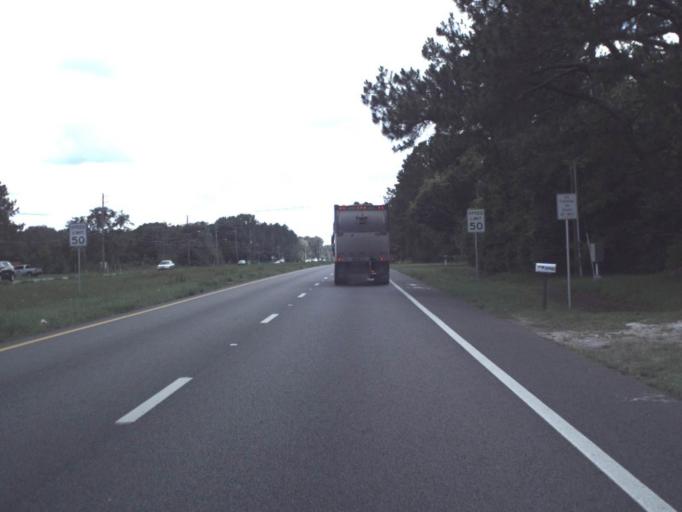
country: US
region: Florida
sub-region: Clay County
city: Bellair-Meadowbrook Terrace
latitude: 30.2697
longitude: -81.8439
